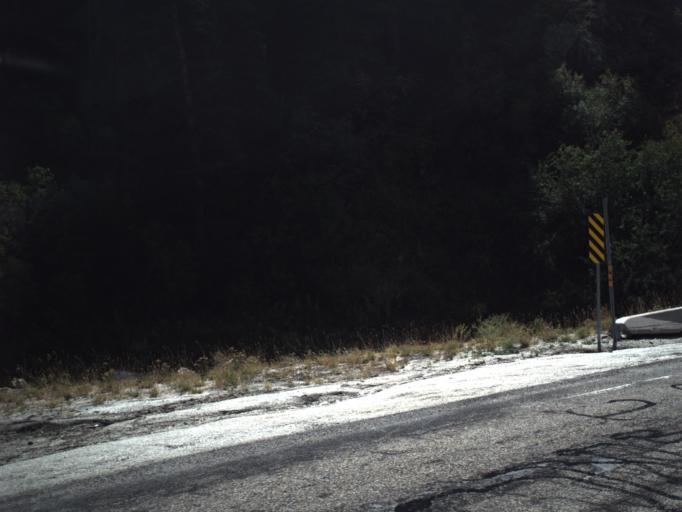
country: US
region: Utah
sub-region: Weber County
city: Wolf Creek
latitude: 41.3613
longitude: -111.7851
